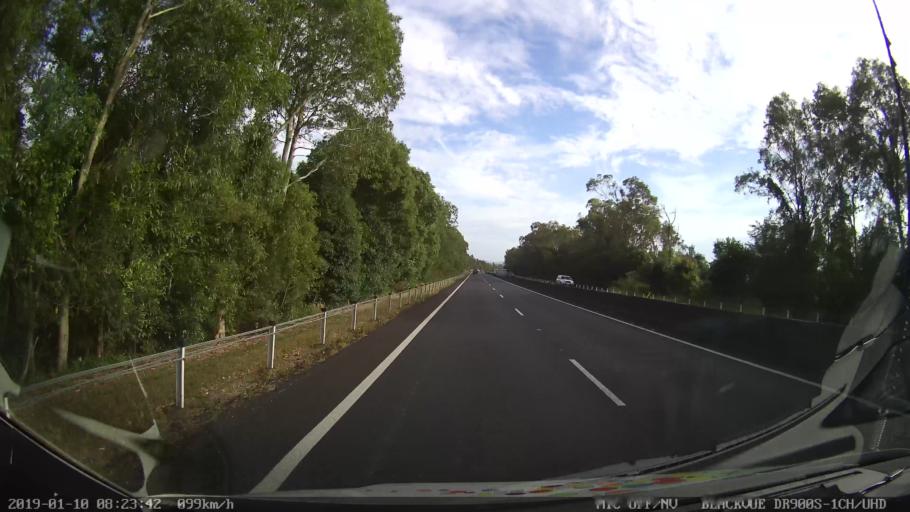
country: AU
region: New South Wales
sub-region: Coffs Harbour
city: Bonville
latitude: -30.4556
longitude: 153.0028
